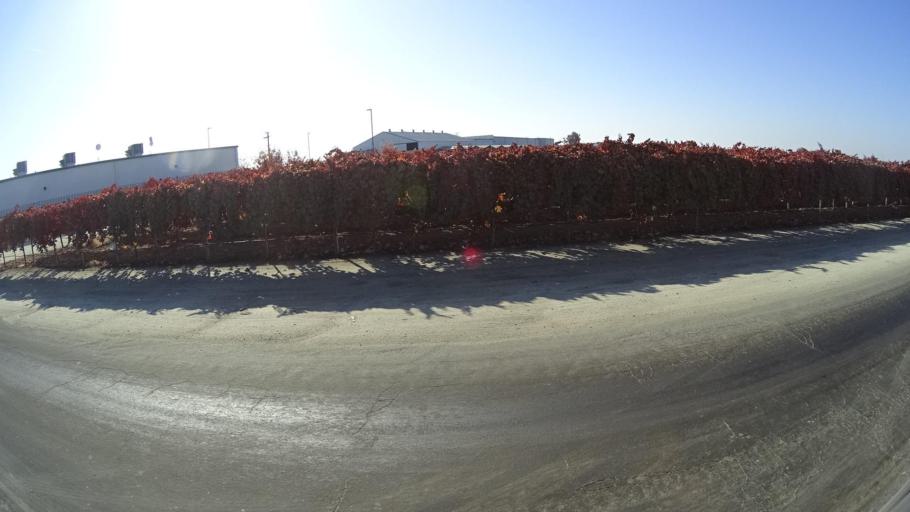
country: US
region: California
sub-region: Tulare County
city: Richgrove
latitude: 35.7471
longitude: -119.1423
